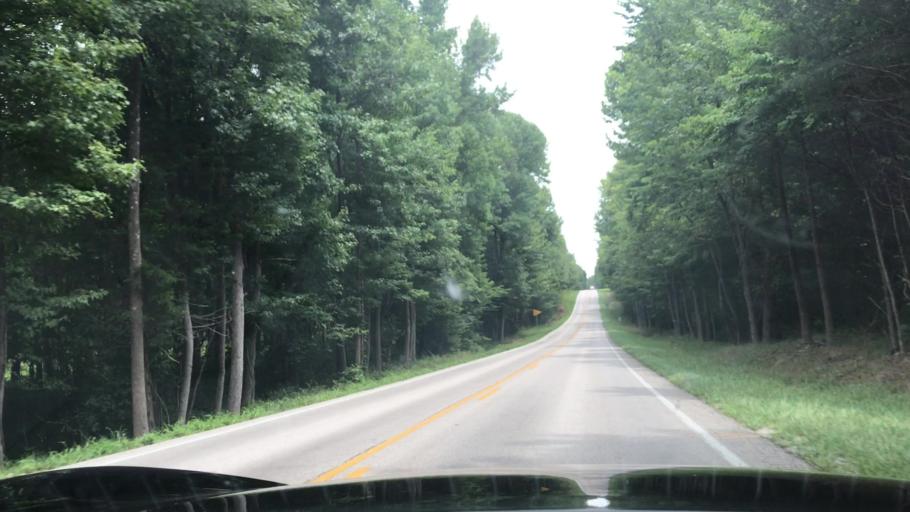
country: US
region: Kentucky
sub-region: Butler County
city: Morgantown
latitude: 37.1778
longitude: -86.8009
